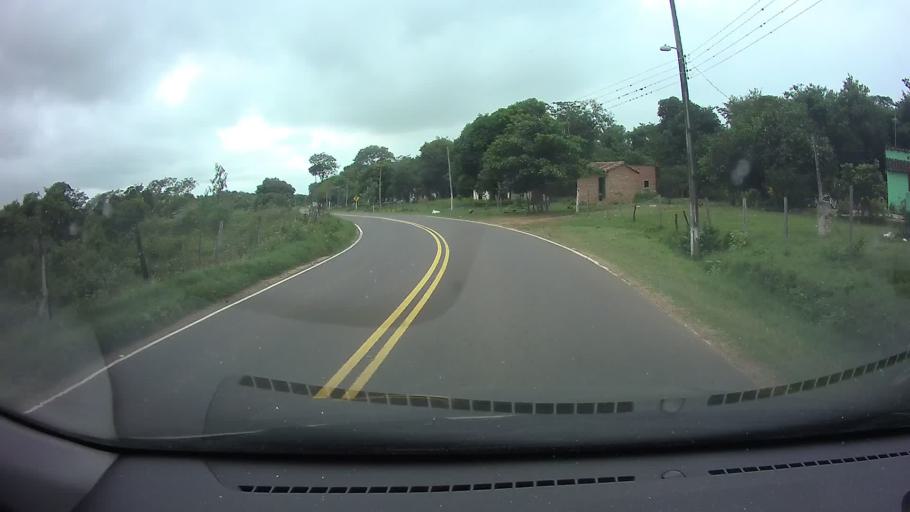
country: PY
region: Central
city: Nueva Italia
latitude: -25.6130
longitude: -57.4047
